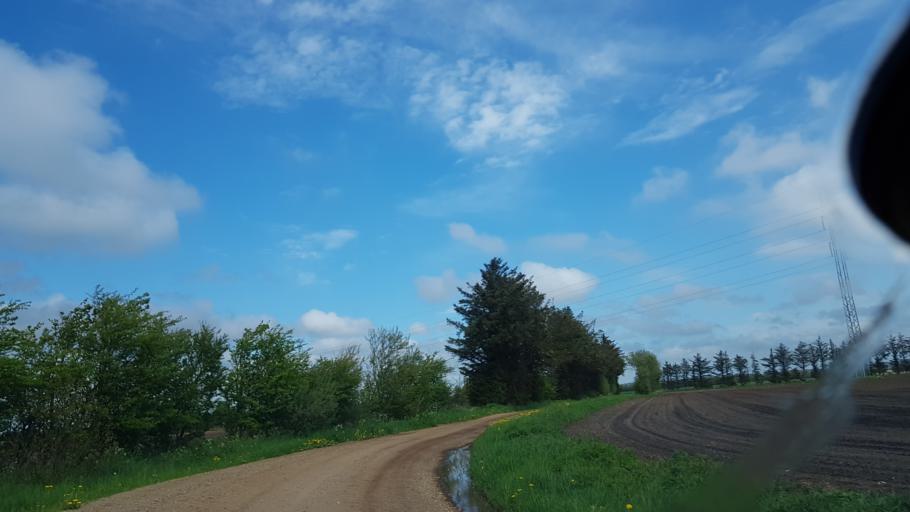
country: DK
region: South Denmark
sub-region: Tonder Kommune
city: Sherrebek
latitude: 55.0843
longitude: 8.8407
